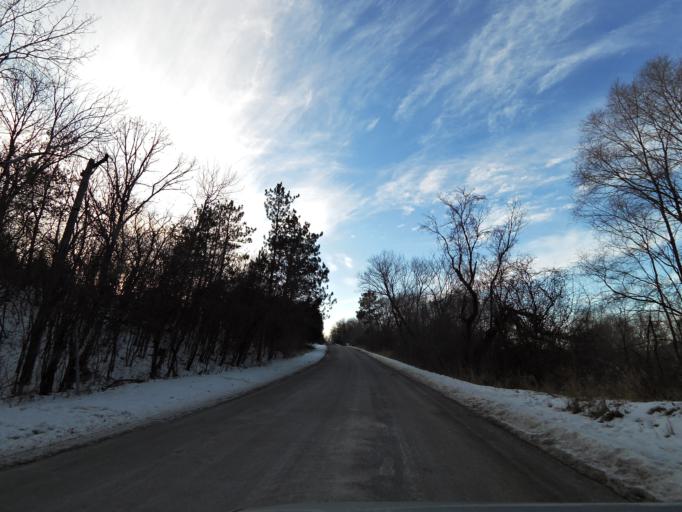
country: US
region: Minnesota
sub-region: Washington County
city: Afton
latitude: 44.9345
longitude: -92.8112
